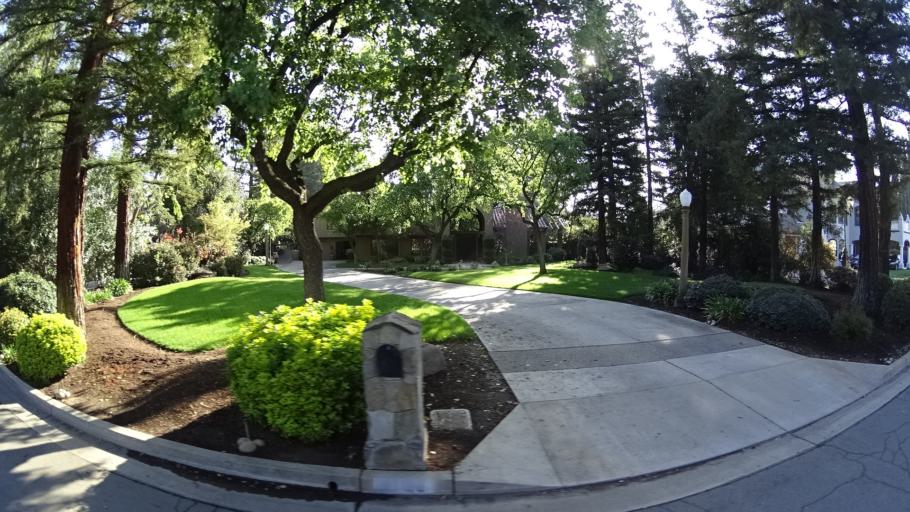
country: US
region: California
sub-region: Fresno County
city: Fresno
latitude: 36.8238
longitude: -119.8331
